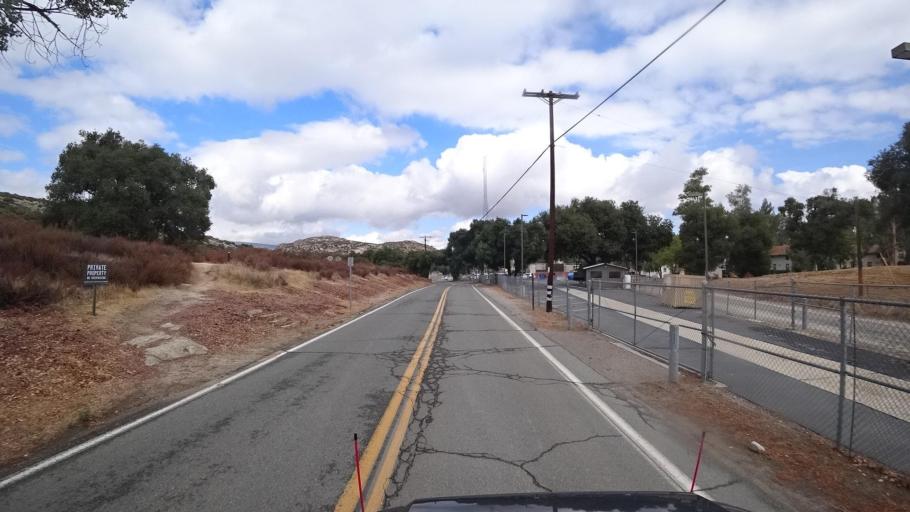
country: US
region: California
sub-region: San Diego County
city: Campo
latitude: 32.6053
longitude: -116.4713
